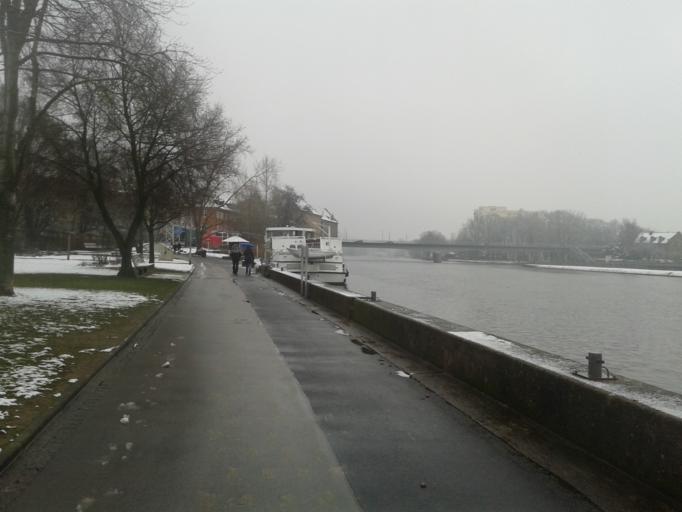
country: DE
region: Bavaria
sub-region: Regierungsbezirk Unterfranken
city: Schweinfurt
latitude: 50.0420
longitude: 10.2336
